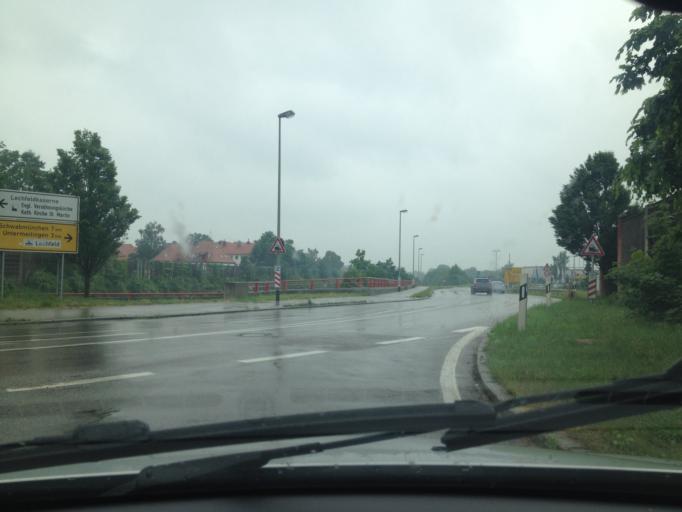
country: DE
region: Bavaria
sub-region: Swabia
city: Klosterlechfeld
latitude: 48.1742
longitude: 10.8399
